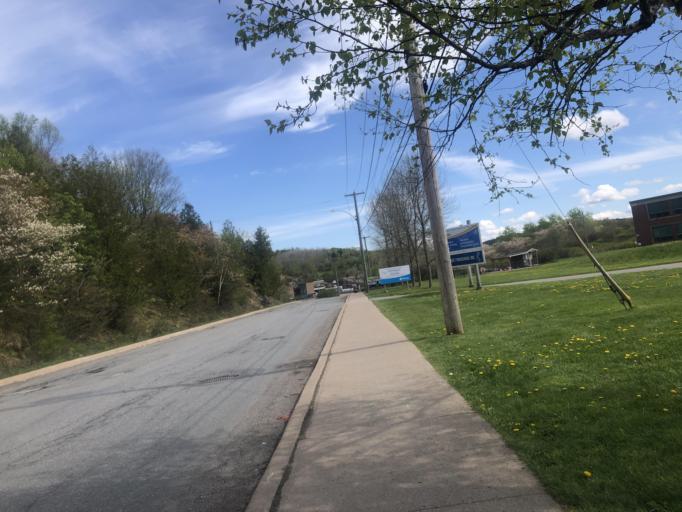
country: CA
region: New Brunswick
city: Saint John
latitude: 45.2857
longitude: -66.0822
